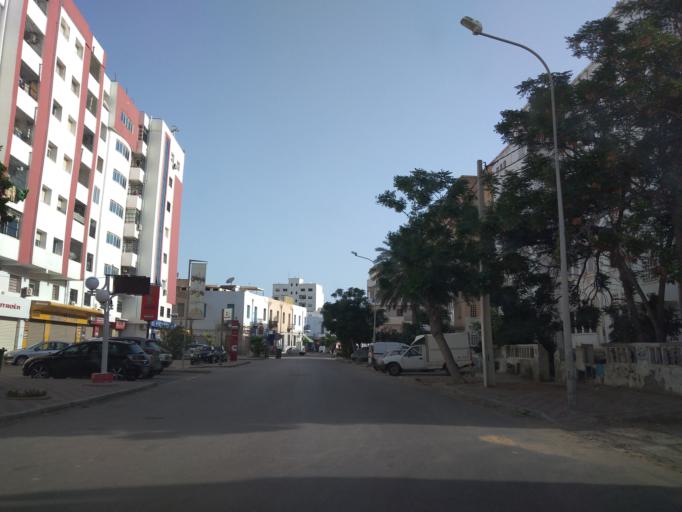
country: TN
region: Safaqis
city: Sfax
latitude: 34.7309
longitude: 10.7549
